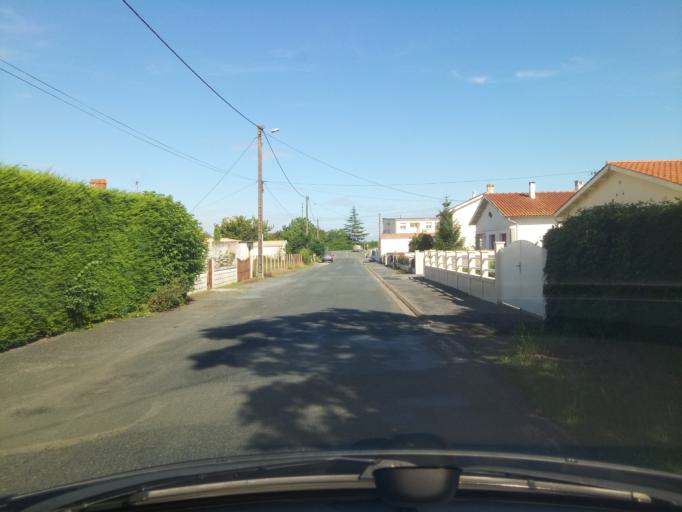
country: FR
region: Poitou-Charentes
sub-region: Departement de la Charente-Maritime
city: Marans
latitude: 46.3031
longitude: -0.9916
